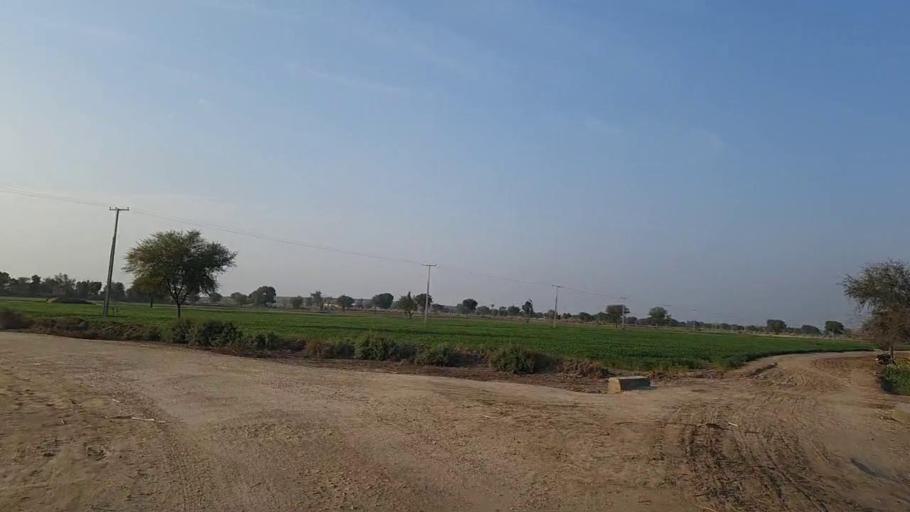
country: PK
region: Sindh
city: Jam Sahib
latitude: 26.3955
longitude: 68.5196
